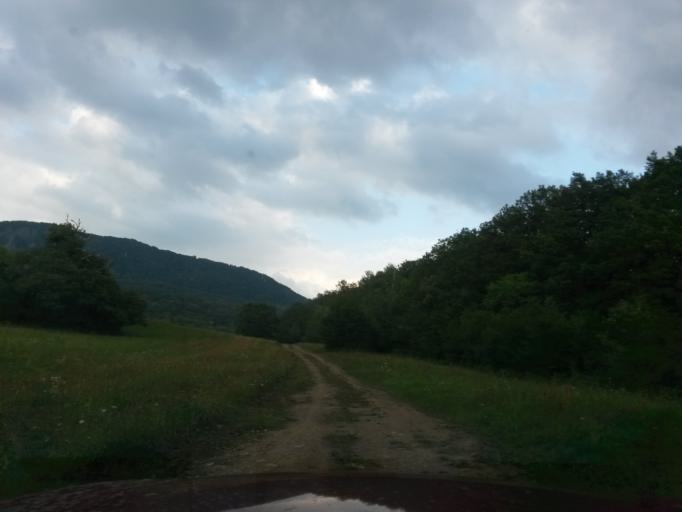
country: SK
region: Kosicky
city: Secovce
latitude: 48.8127
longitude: 21.4799
